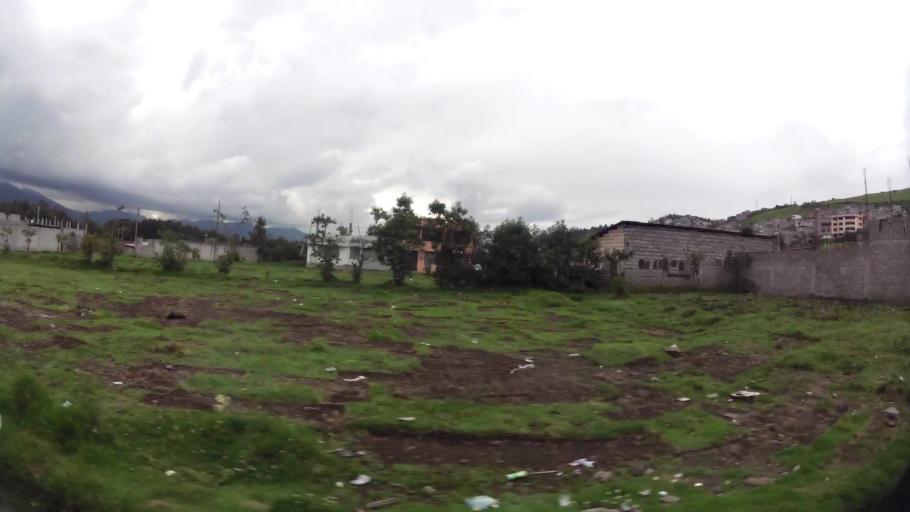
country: EC
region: Pichincha
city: Sangolqui
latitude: -0.3254
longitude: -78.5326
